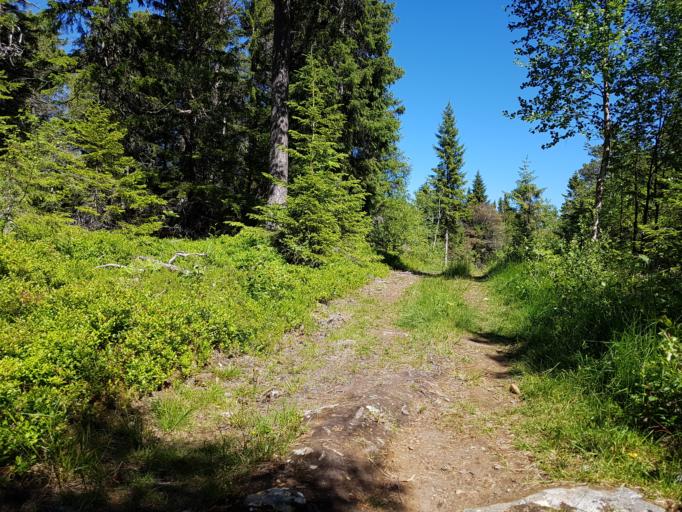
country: NO
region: Sor-Trondelag
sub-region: Melhus
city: Melhus
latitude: 63.4348
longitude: 10.2041
